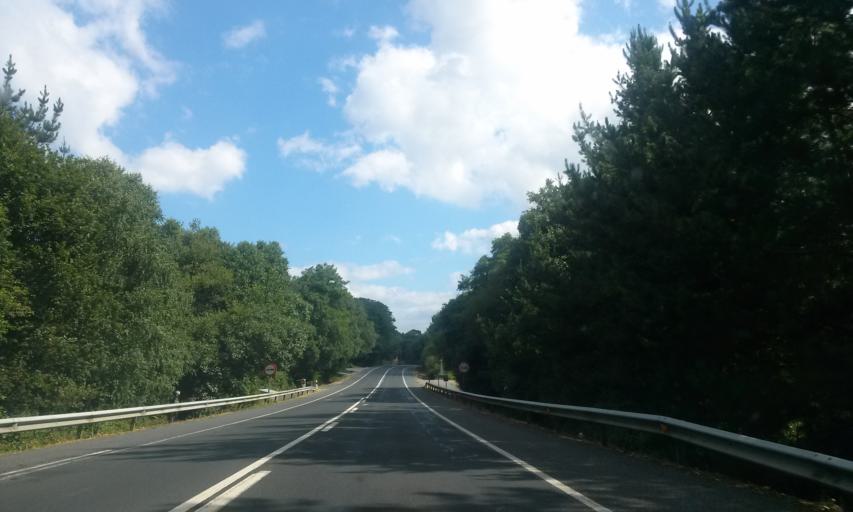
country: ES
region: Galicia
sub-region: Provincia de Lugo
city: Outeiro de Rei
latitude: 43.0925
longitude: -7.6074
